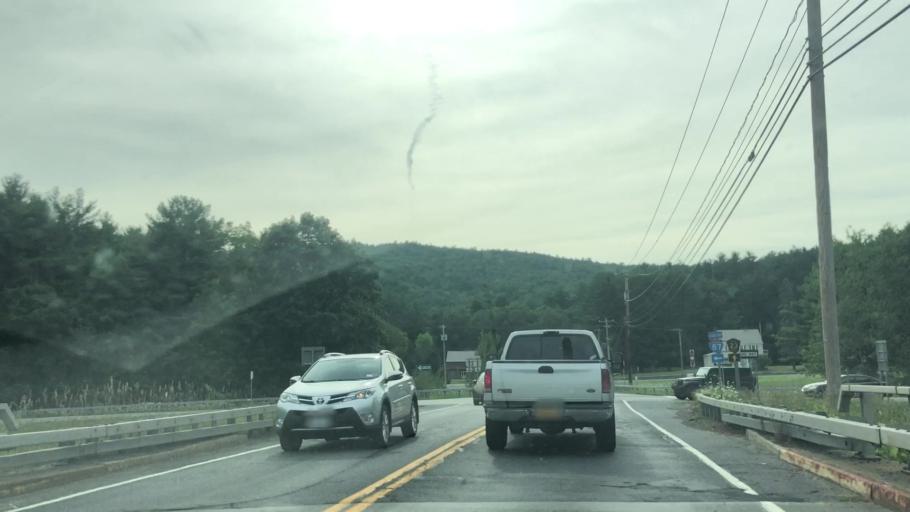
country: US
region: New York
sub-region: Warren County
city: Glens Falls North
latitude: 43.3592
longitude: -73.7046
